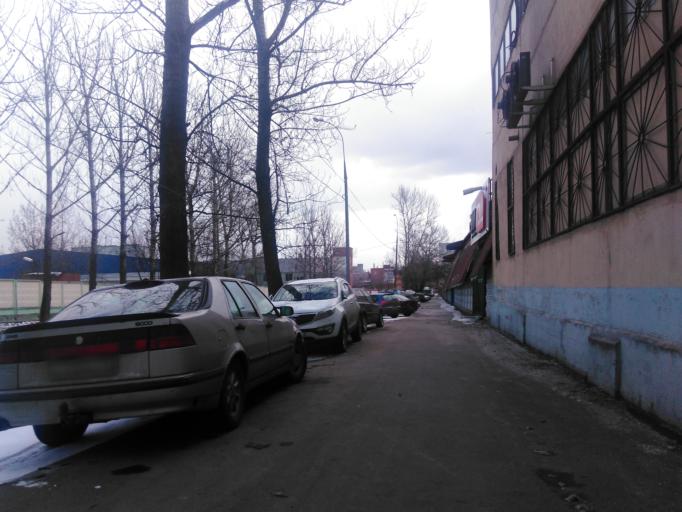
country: RU
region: Moscow
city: Nagornyy
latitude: 55.6450
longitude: 37.6351
